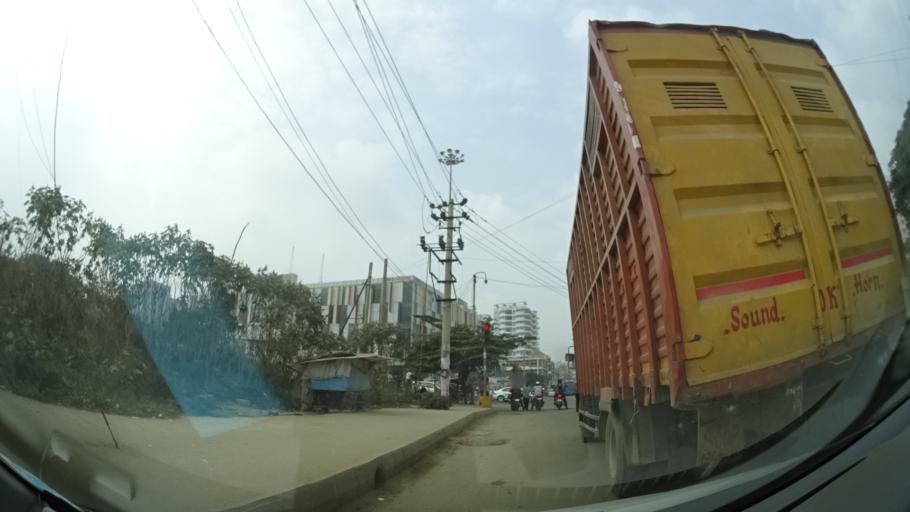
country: IN
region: Karnataka
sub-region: Bangalore Rural
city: Hoskote
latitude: 12.9837
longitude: 77.7527
